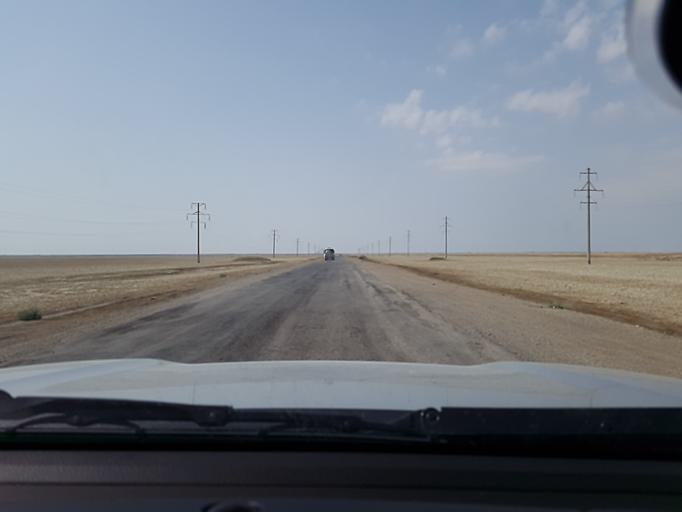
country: TM
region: Balkan
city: Gumdag
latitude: 39.0681
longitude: 54.5843
